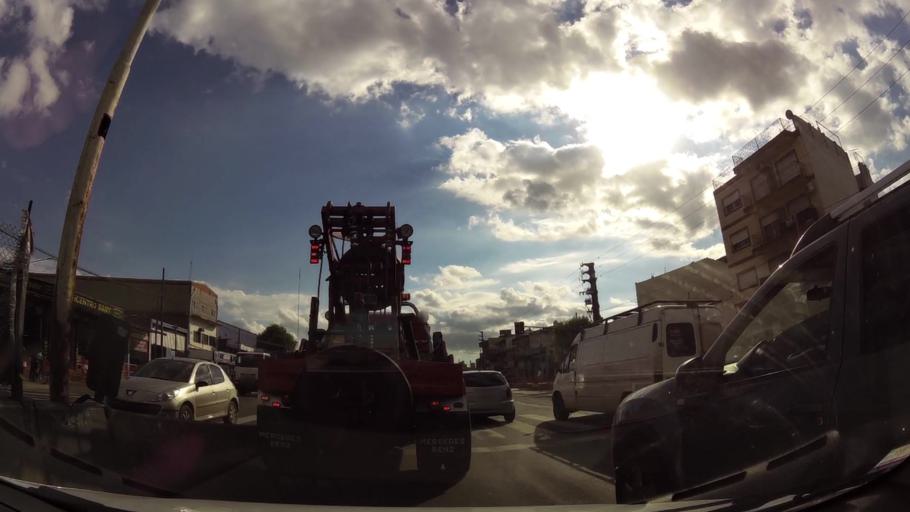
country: AR
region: Buenos Aires
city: San Justo
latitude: -34.6905
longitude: -58.5693
